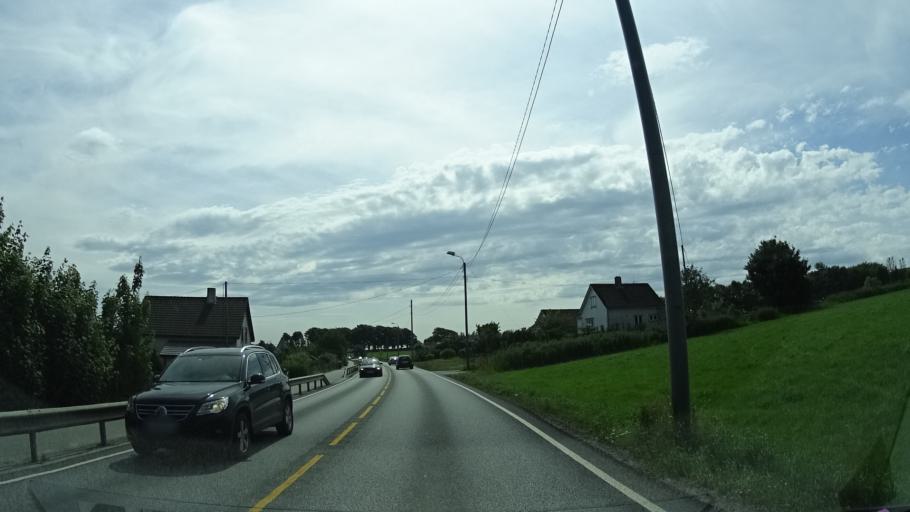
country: NO
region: Rogaland
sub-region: Randaberg
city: Randaberg
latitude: 58.9869
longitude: 5.6652
